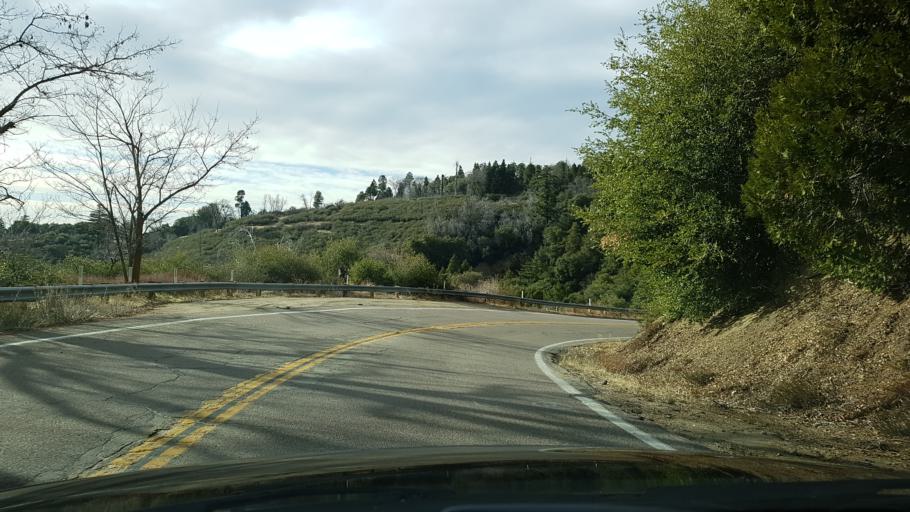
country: US
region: California
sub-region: Riverside County
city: Aguanga
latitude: 33.3134
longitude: -116.8676
